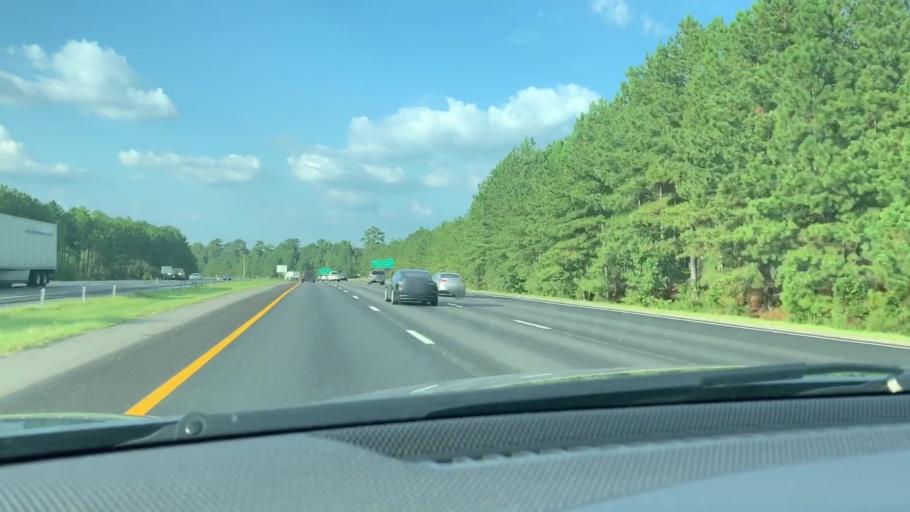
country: US
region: South Carolina
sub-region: Richland County
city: Forest Acres
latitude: 33.9852
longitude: -80.9531
